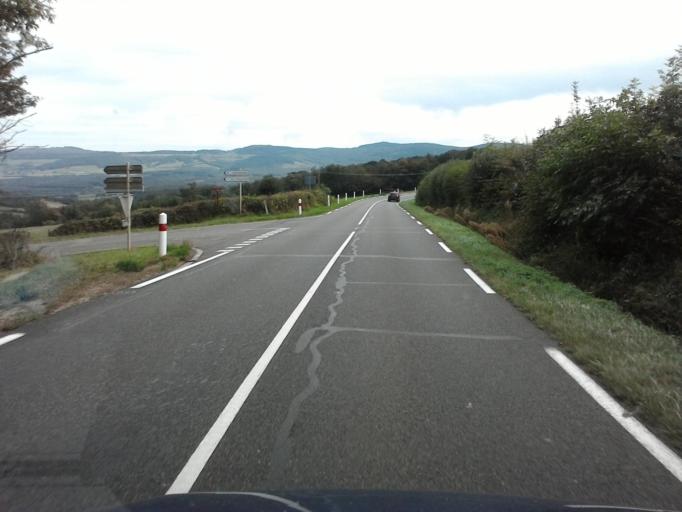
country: FR
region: Bourgogne
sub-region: Departement de Saone-et-Loire
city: Cluny
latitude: 46.4590
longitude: 4.6296
